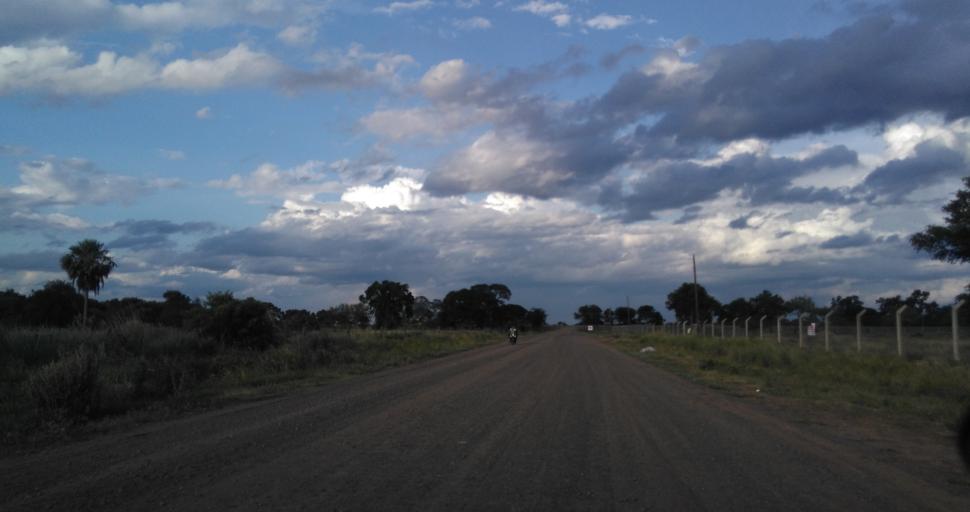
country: AR
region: Chaco
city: Resistencia
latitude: -27.4147
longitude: -58.9458
